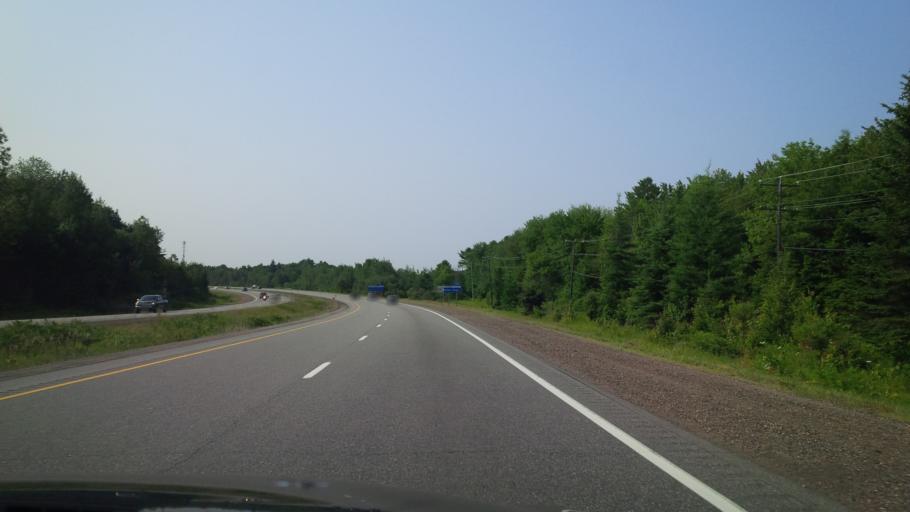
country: CA
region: Ontario
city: Bracebridge
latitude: 45.0657
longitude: -79.2974
